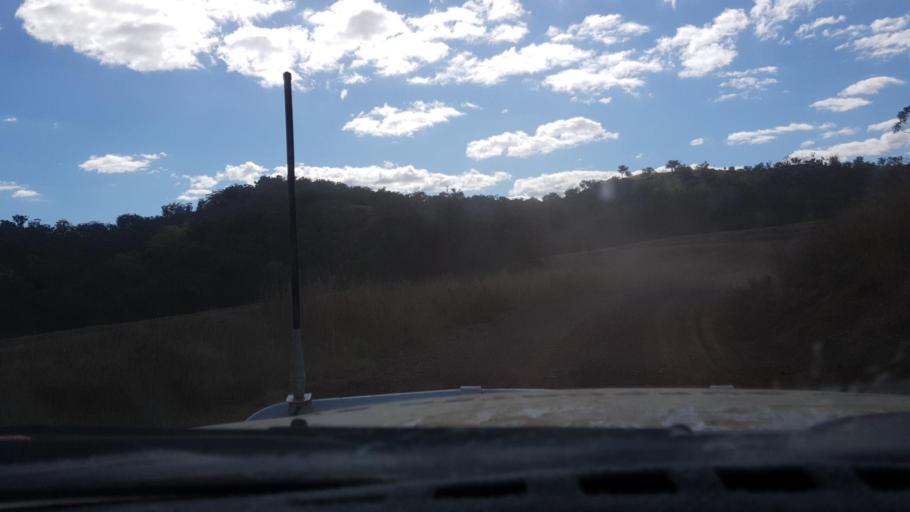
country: AU
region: New South Wales
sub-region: Tamworth Municipality
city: Manilla
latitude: -30.4345
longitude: 150.7899
